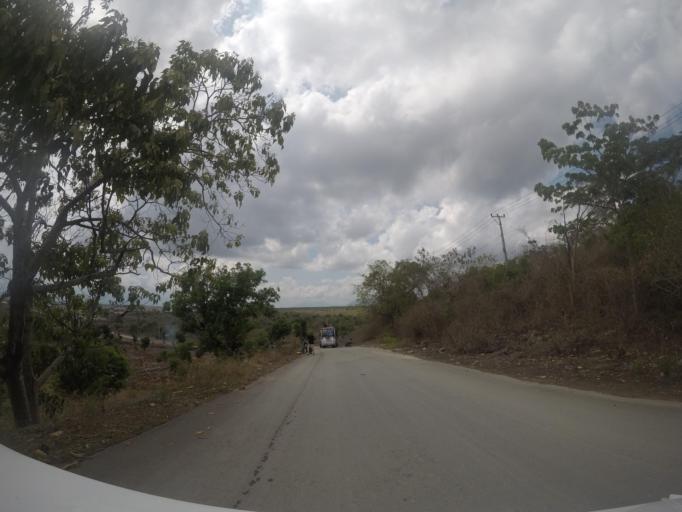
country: TL
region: Baucau
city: Baucau
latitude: -8.4686
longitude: 126.4340
